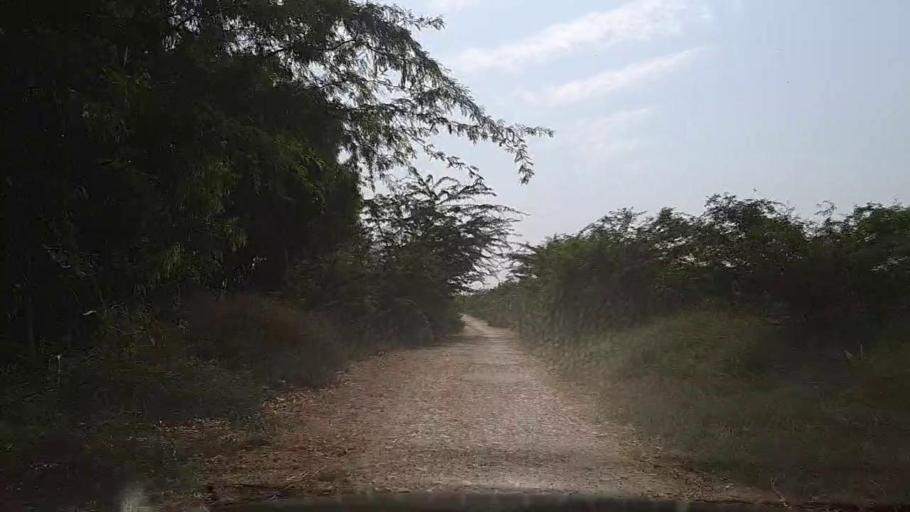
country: PK
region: Sindh
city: Thatta
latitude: 24.7587
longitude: 67.7781
